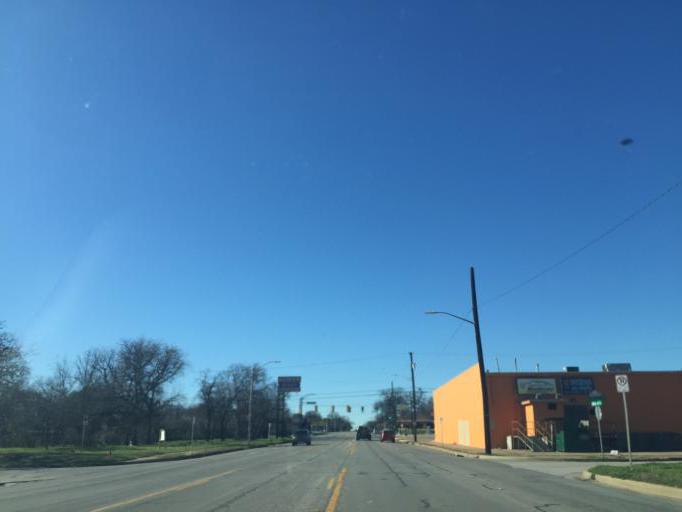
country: US
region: Texas
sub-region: Tarrant County
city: River Oaks
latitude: 32.7753
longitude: -97.3474
